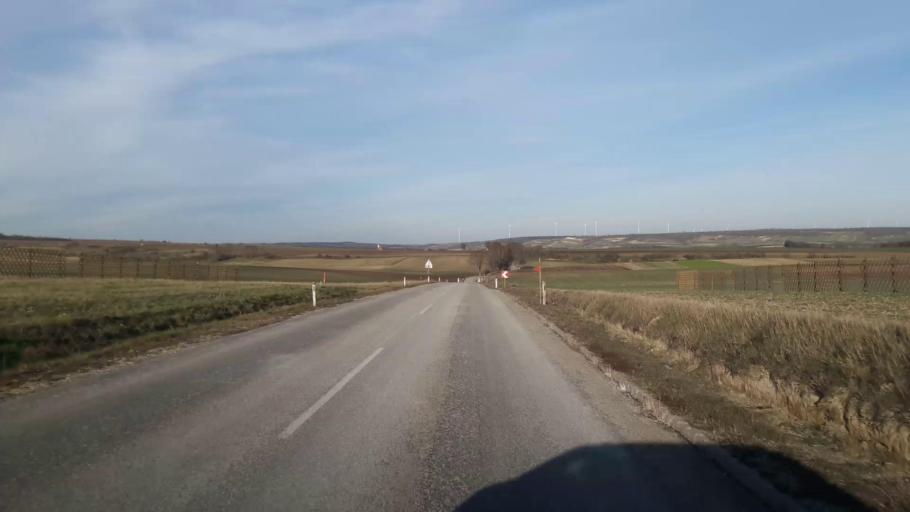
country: AT
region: Lower Austria
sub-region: Politischer Bezirk Ganserndorf
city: Auersthal
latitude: 48.3851
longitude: 16.6306
